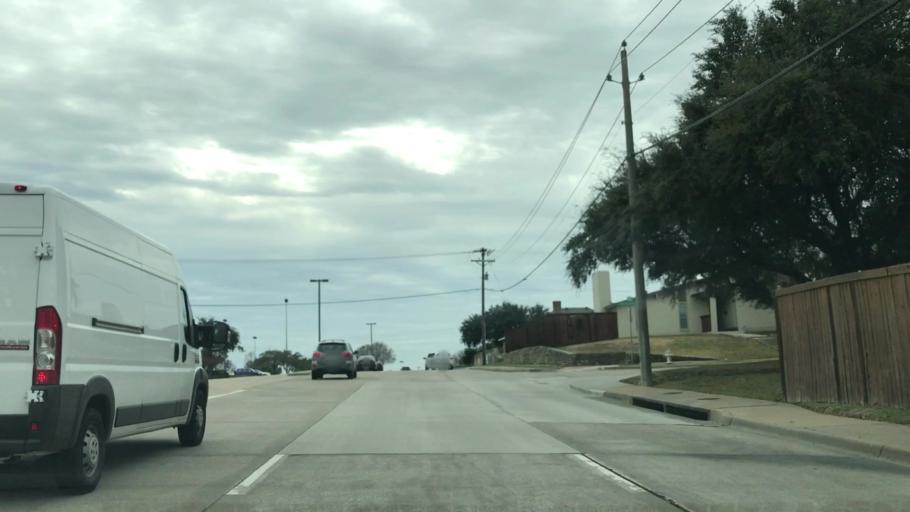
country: US
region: Texas
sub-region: Dallas County
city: Carrollton
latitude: 32.9926
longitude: -96.8899
